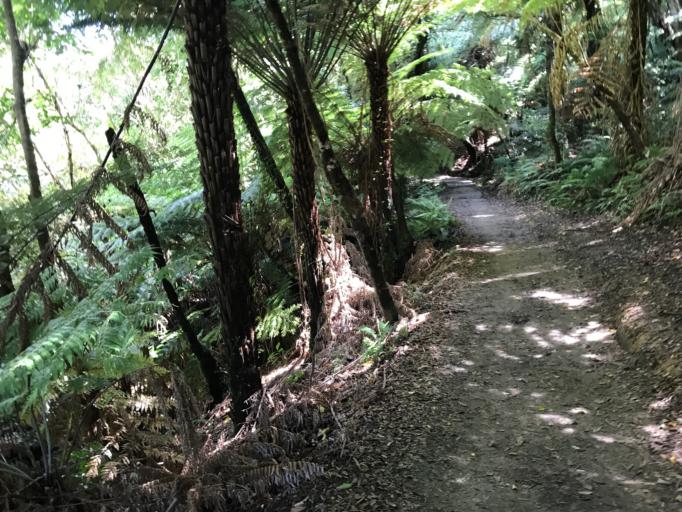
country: NZ
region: Marlborough
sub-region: Marlborough District
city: Picton
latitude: -41.2617
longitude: 173.9298
